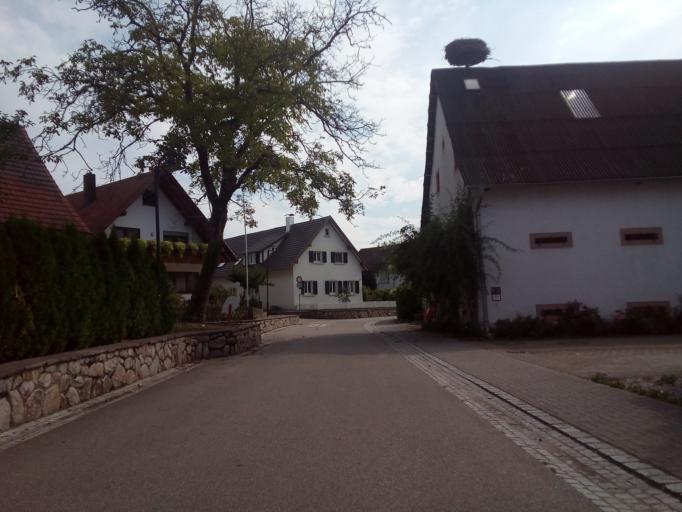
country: DE
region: Baden-Wuerttemberg
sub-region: Freiburg Region
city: Sasbach
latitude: 48.6588
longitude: 8.0853
